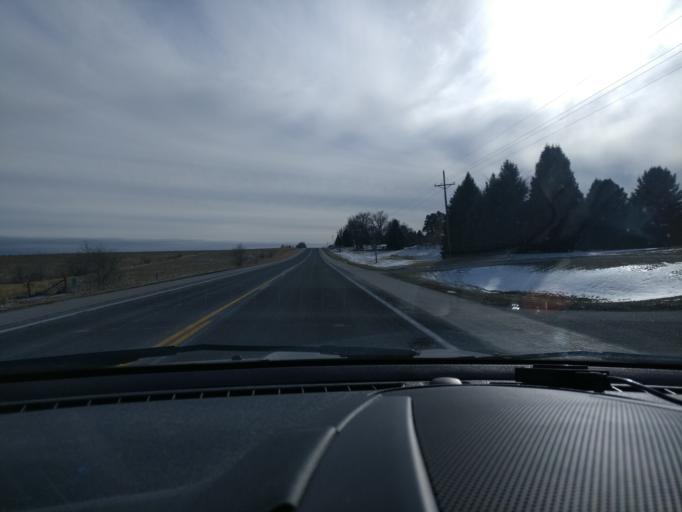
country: US
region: Nebraska
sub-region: Dodge County
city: Fremont
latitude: 41.3181
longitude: -96.5025
